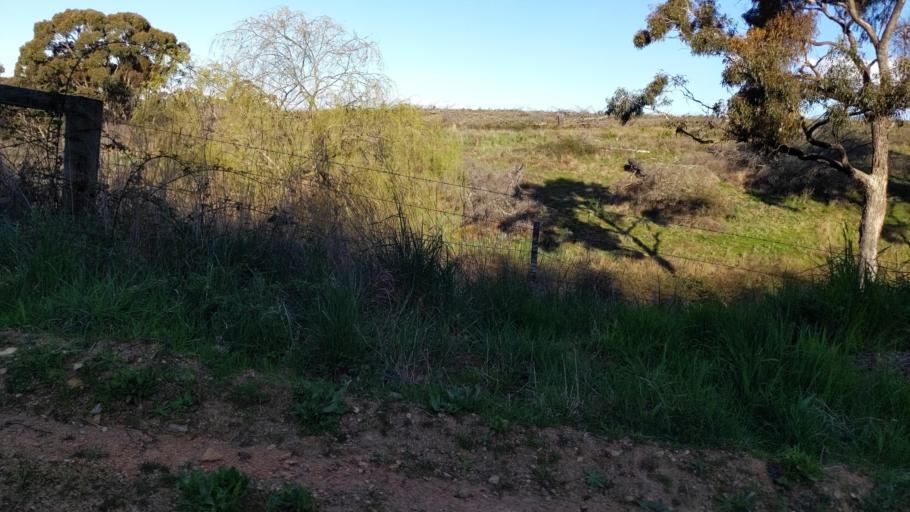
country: AU
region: New South Wales
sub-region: Blayney
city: Millthorpe
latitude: -33.4040
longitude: 149.3127
